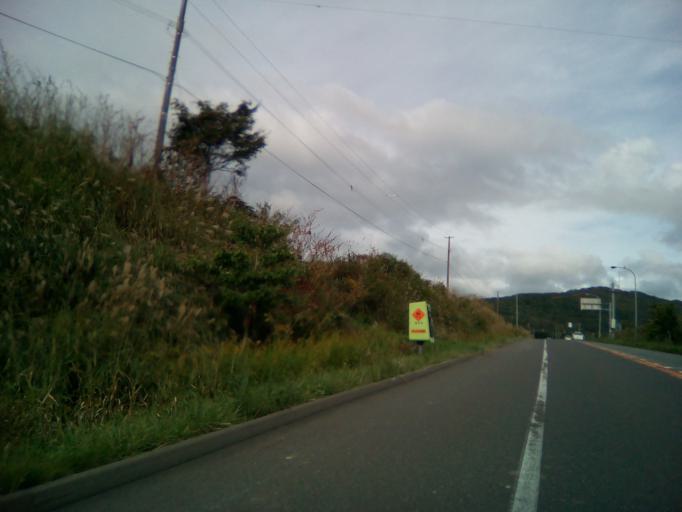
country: JP
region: Hokkaido
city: Niseko Town
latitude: 42.6786
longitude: 140.8373
